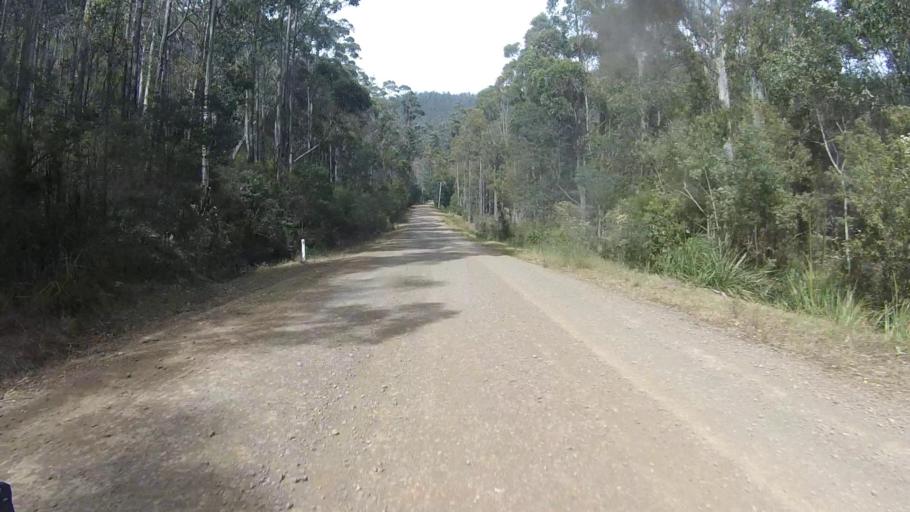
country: AU
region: Tasmania
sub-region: Sorell
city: Sorell
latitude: -42.6905
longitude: 147.8649
